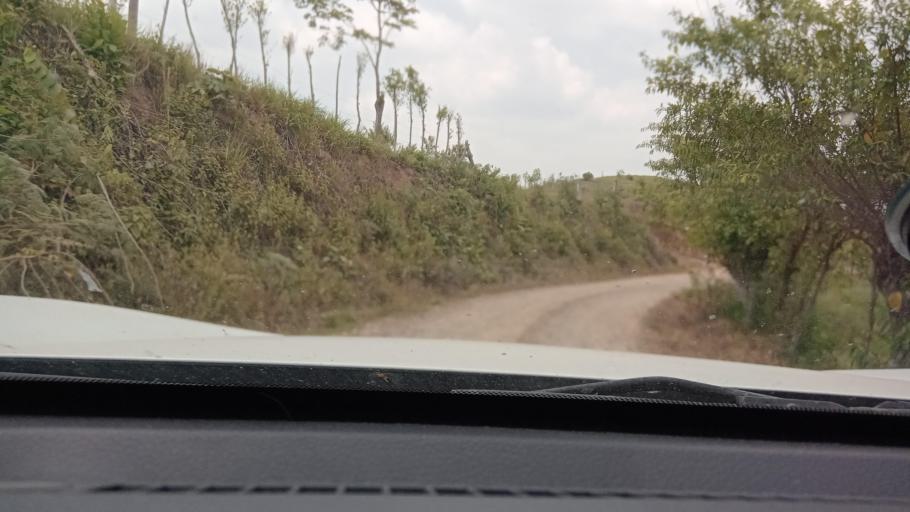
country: MX
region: Tabasco
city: Chontalpa
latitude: 17.5738
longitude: -93.7095
